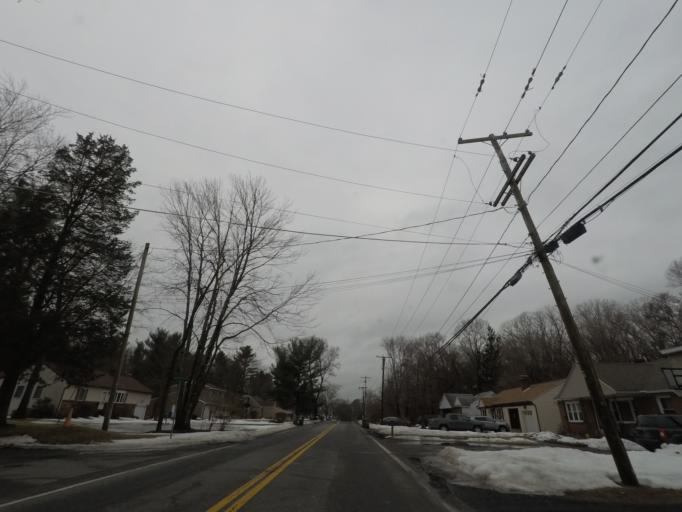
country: US
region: New York
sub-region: Albany County
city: Westmere
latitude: 42.6944
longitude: -73.8648
